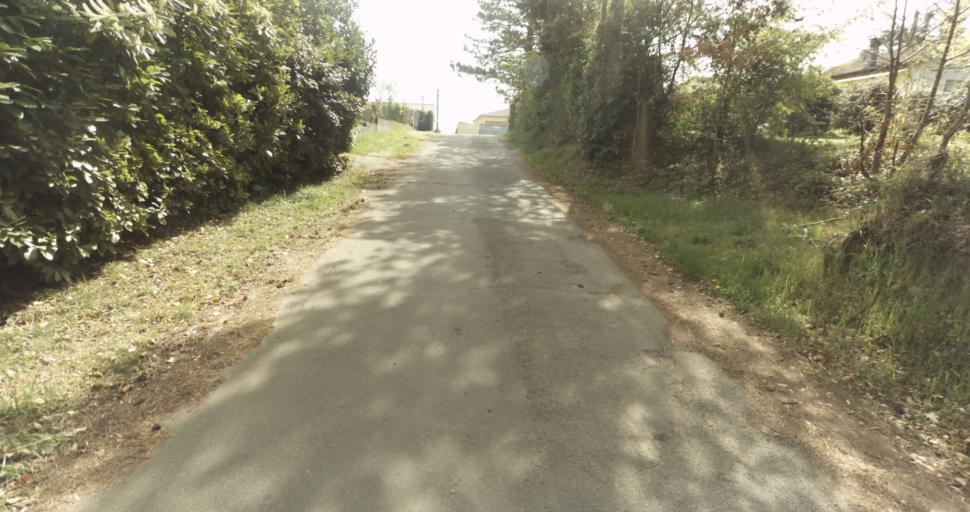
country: FR
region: Midi-Pyrenees
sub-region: Departement du Tarn-et-Garonne
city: Moissac
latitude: 44.1135
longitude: 1.0723
